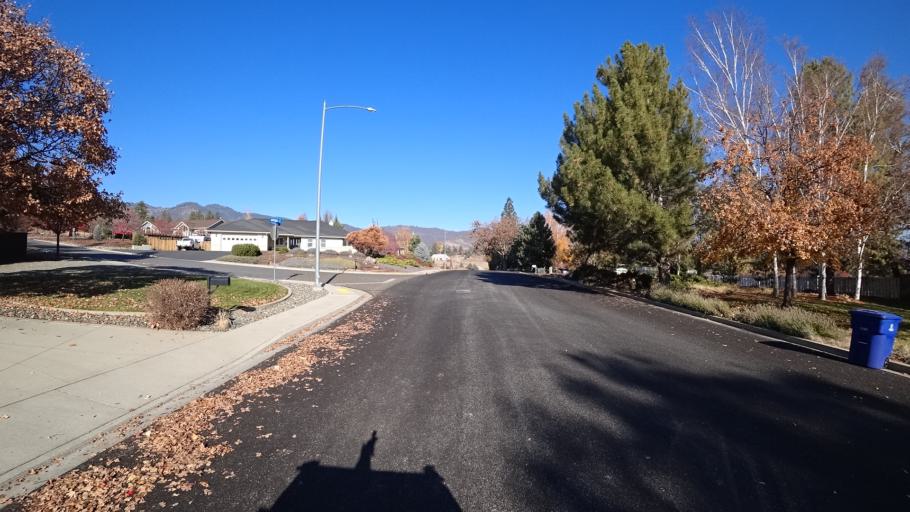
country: US
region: California
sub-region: Siskiyou County
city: Yreka
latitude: 41.7244
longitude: -122.6504
